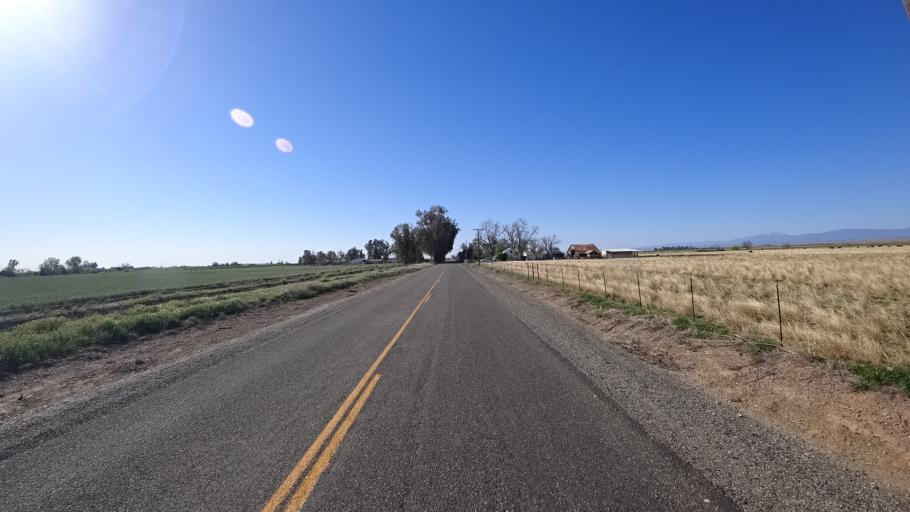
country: US
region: California
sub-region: Glenn County
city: Orland
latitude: 39.7582
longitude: -122.2479
